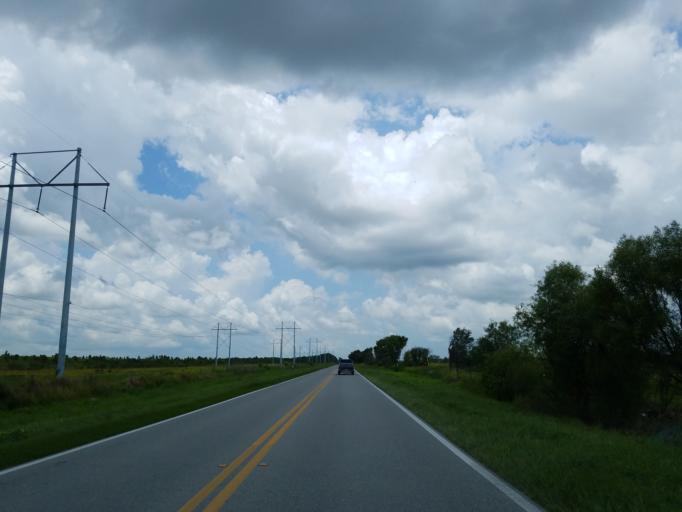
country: US
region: Florida
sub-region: Polk County
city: Fuller Heights
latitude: 27.8508
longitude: -82.0288
